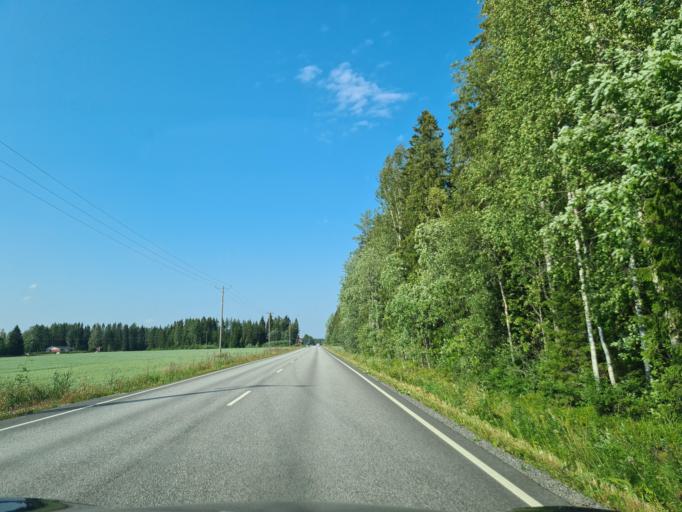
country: FI
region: Satakunta
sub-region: Pohjois-Satakunta
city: Kankaanpaeae
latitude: 61.9107
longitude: 22.5010
